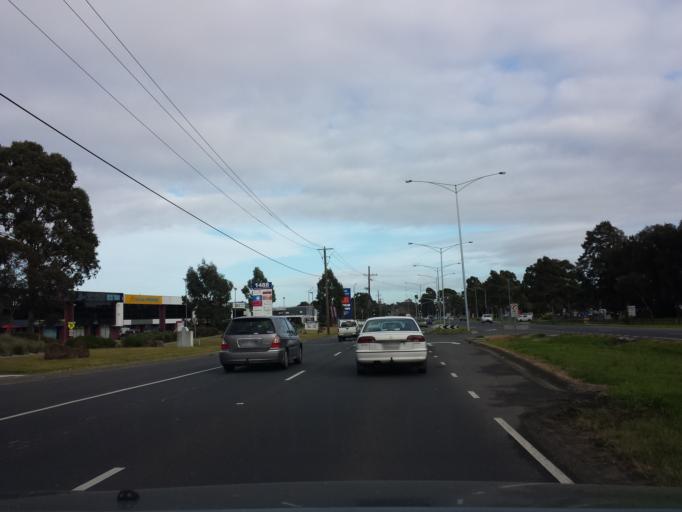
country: AU
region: Victoria
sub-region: Knox
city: Knoxfield
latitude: -37.8975
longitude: 145.2450
